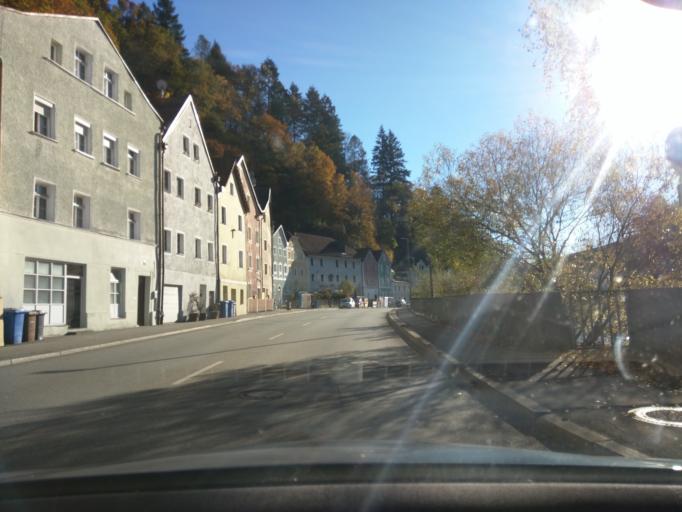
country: DE
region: Bavaria
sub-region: Lower Bavaria
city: Salzweg
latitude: 48.5803
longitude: 13.4765
